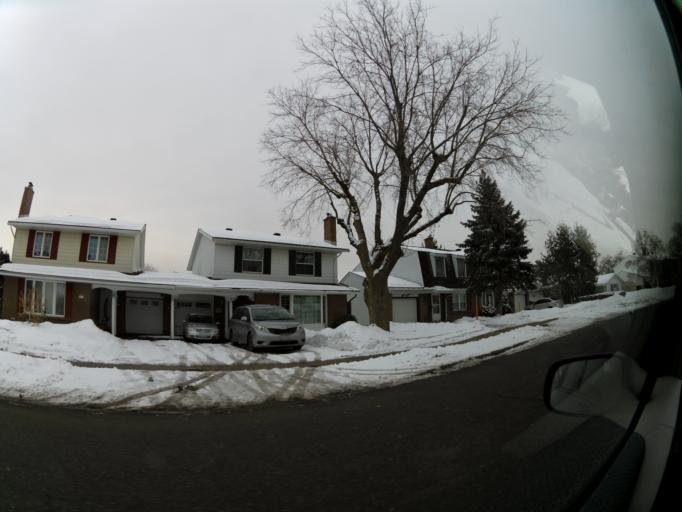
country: CA
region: Quebec
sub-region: Outaouais
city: Gatineau
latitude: 45.4535
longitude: -75.5937
